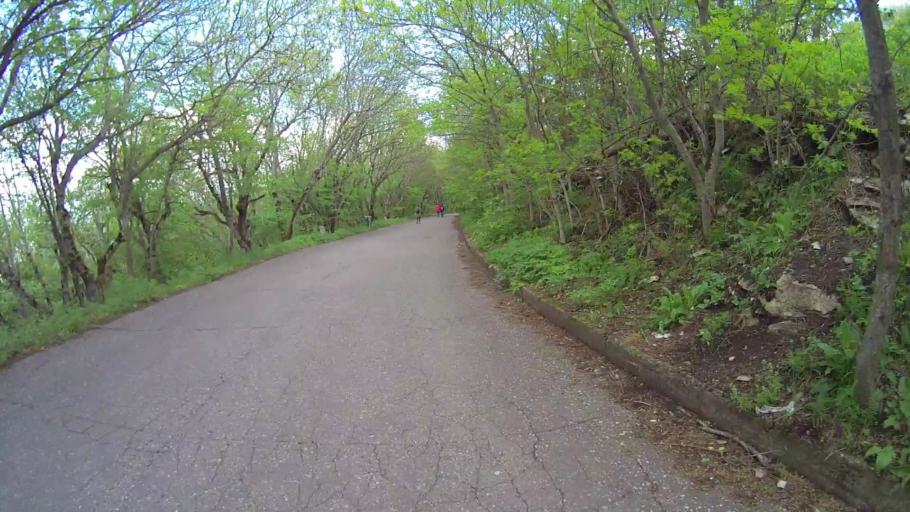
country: RU
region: Stavropol'skiy
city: Goryachevodskiy
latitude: 44.0520
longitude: 43.0886
